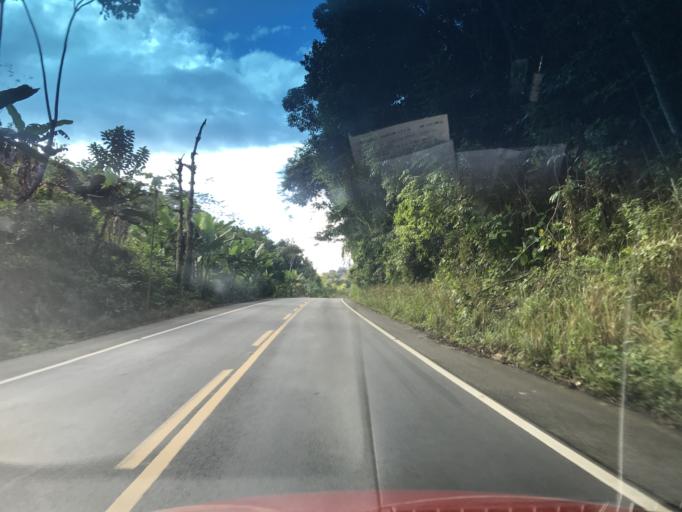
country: BR
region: Bahia
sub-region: Ibirapitanga
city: Ibirapitanga
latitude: -14.1914
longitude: -39.3156
